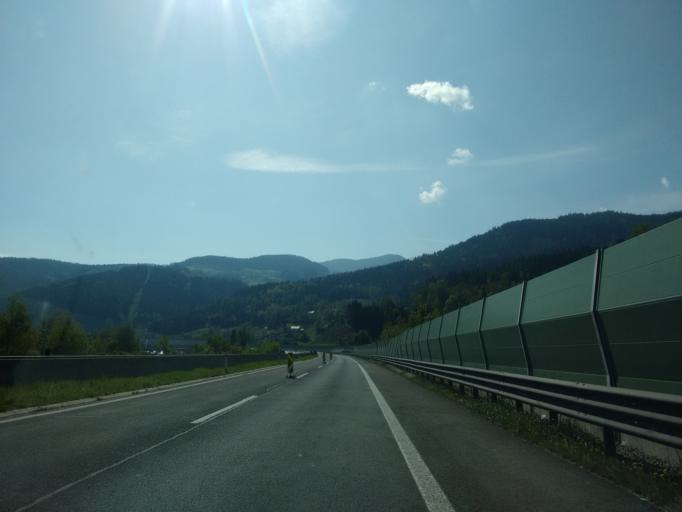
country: AT
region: Styria
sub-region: Politischer Bezirk Bruck-Muerzzuschlag
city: Oberaich
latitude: 47.4008
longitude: 15.2247
